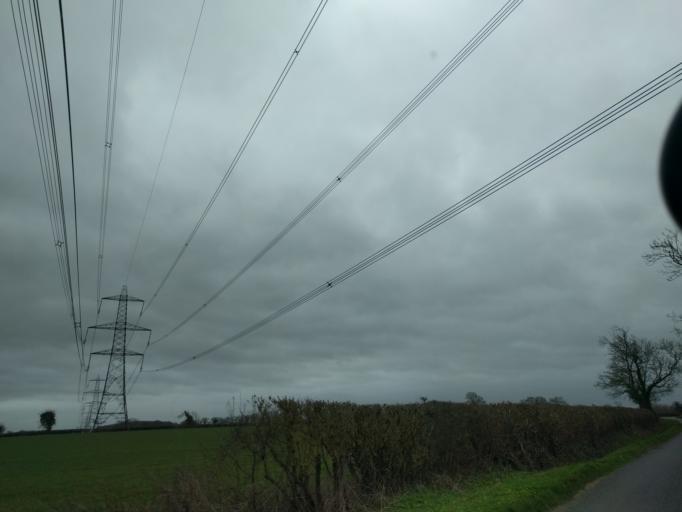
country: GB
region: England
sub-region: Wiltshire
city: Biddestone
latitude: 51.4766
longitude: -2.1961
